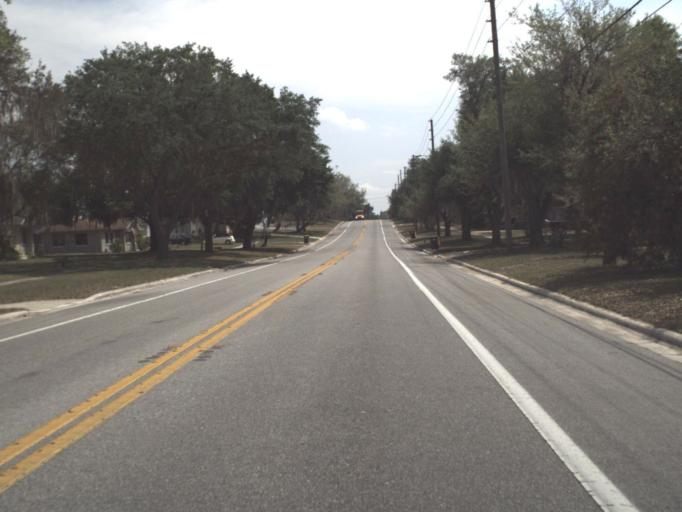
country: US
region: Florida
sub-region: Lake County
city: Howie In The Hills
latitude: 28.7117
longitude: -81.7721
